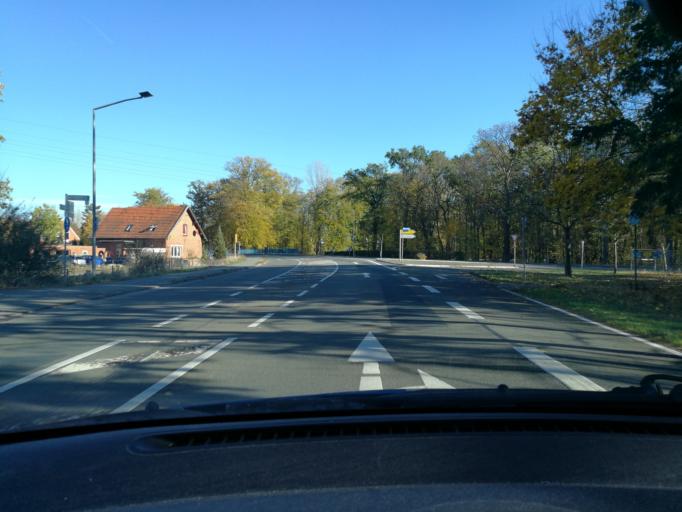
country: DE
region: Lower Saxony
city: Dannenberg
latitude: 53.0870
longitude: 11.0819
